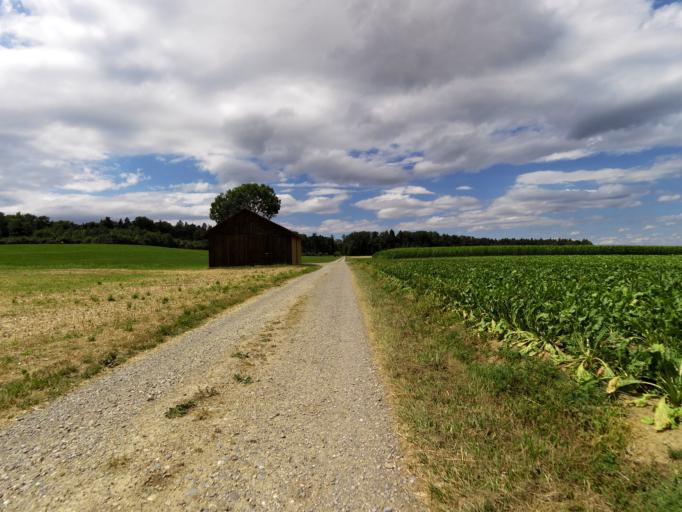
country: CH
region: Thurgau
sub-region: Kreuzlingen District
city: Ermatingen
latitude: 47.6510
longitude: 9.0842
